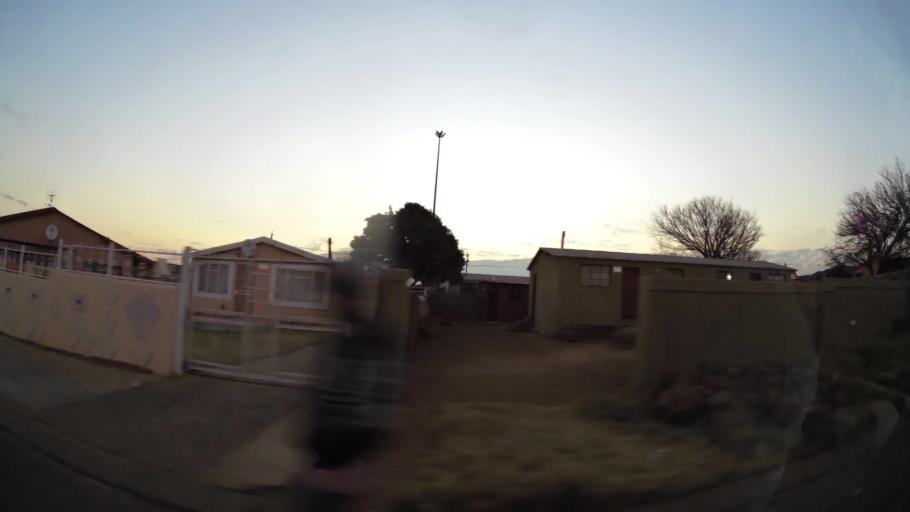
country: ZA
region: Gauteng
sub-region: West Rand District Municipality
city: Randfontein
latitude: -26.2072
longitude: 27.7149
